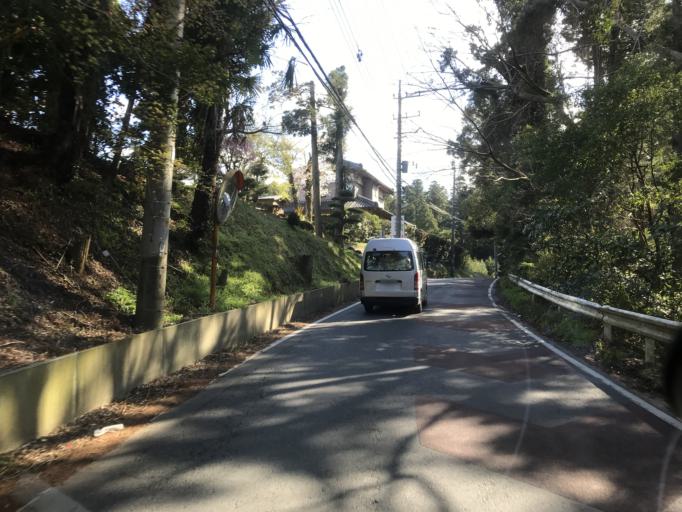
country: JP
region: Chiba
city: Sawara
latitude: 35.8409
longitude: 140.4298
